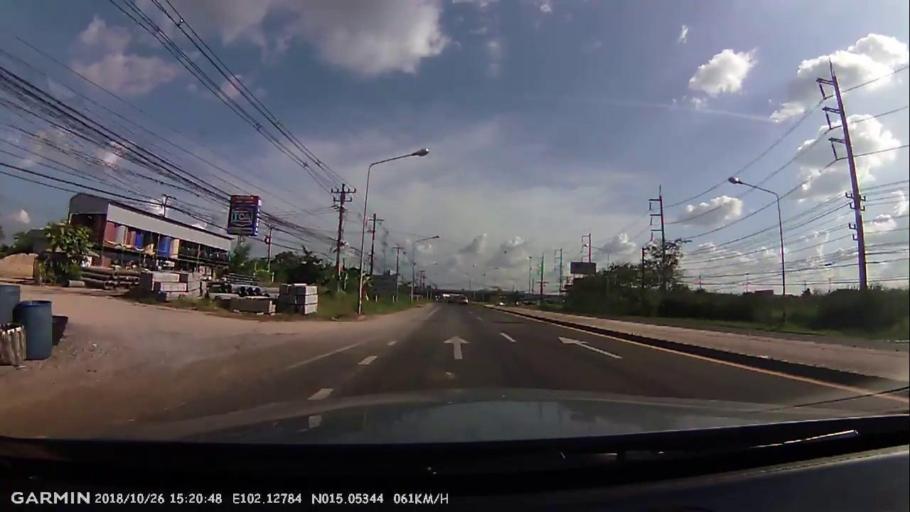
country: TH
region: Nakhon Ratchasima
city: Nakhon Ratchasima
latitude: 15.0535
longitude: 102.1279
